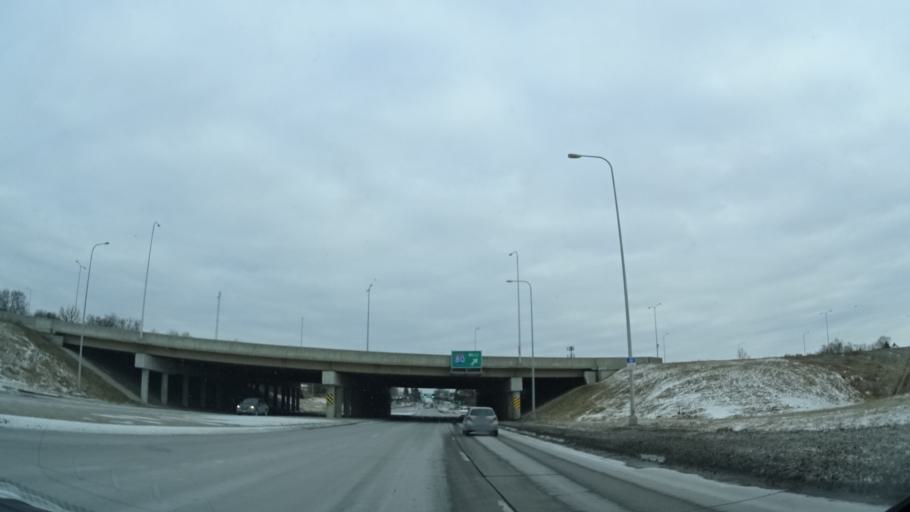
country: US
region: Nebraska
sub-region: Douglas County
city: Omaha
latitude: 41.2237
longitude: -95.9757
